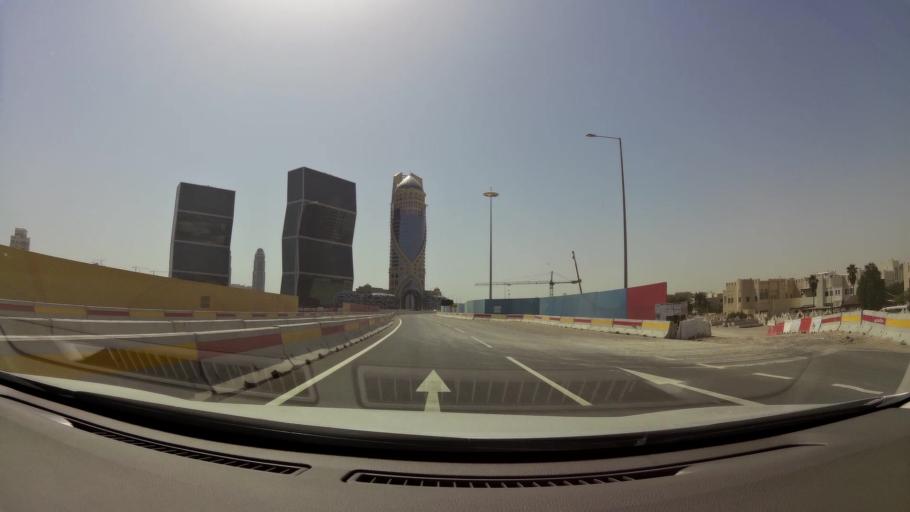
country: QA
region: Baladiyat ad Dawhah
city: Doha
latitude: 25.3807
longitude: 51.5215
